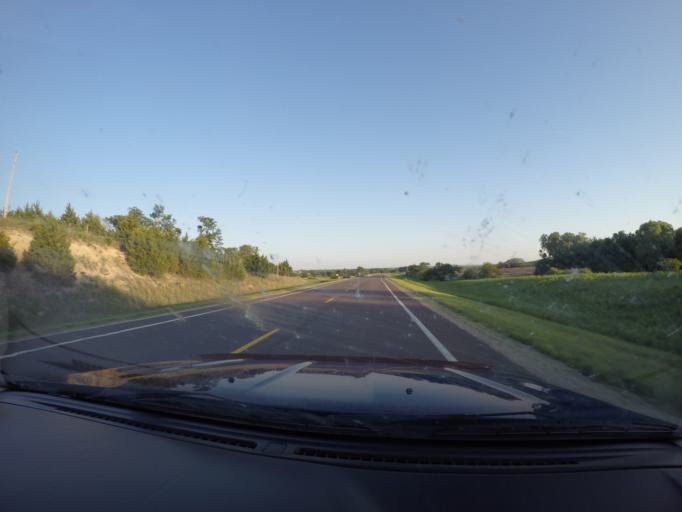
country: US
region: Kansas
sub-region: Marshall County
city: Blue Rapids
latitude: 39.5191
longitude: -96.7551
